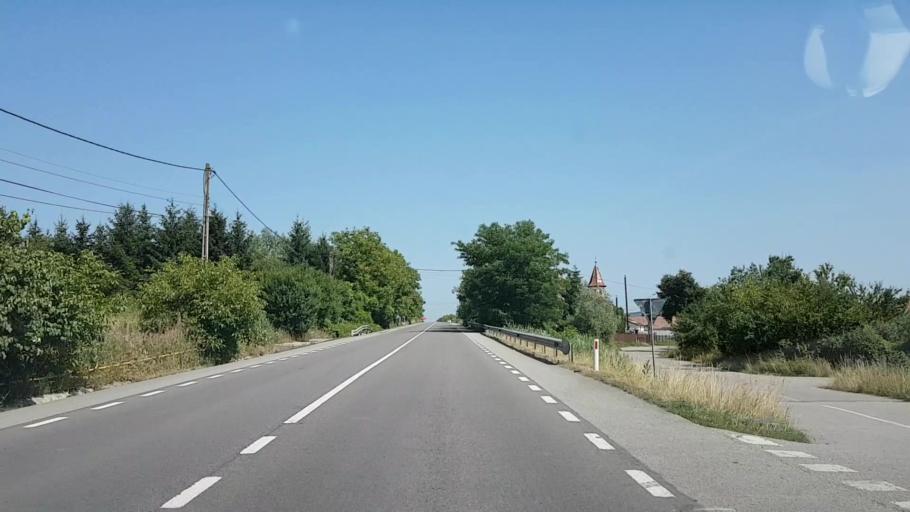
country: RO
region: Bistrita-Nasaud
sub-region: Comuna Uriu
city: Cristestii Ciceului
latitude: 47.1853
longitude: 24.1243
